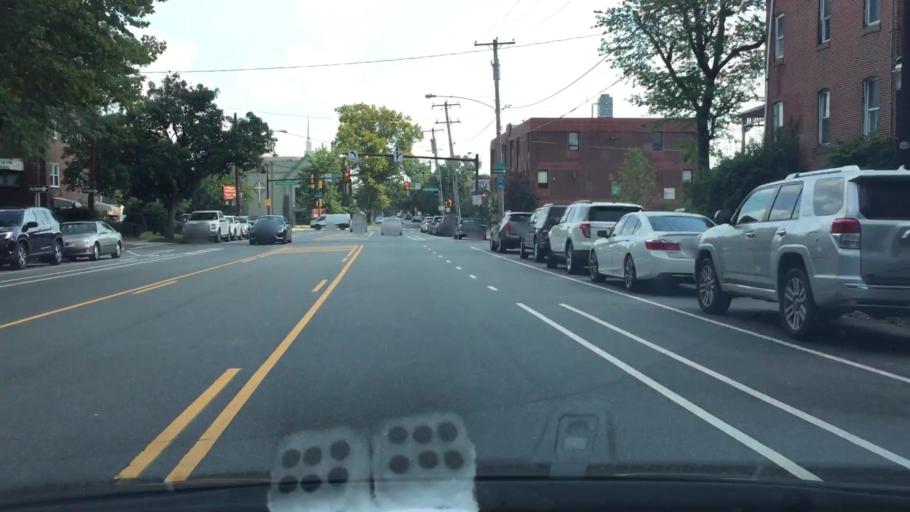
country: US
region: New Jersey
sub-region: Burlington County
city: Palmyra
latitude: 40.0280
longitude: -75.0418
